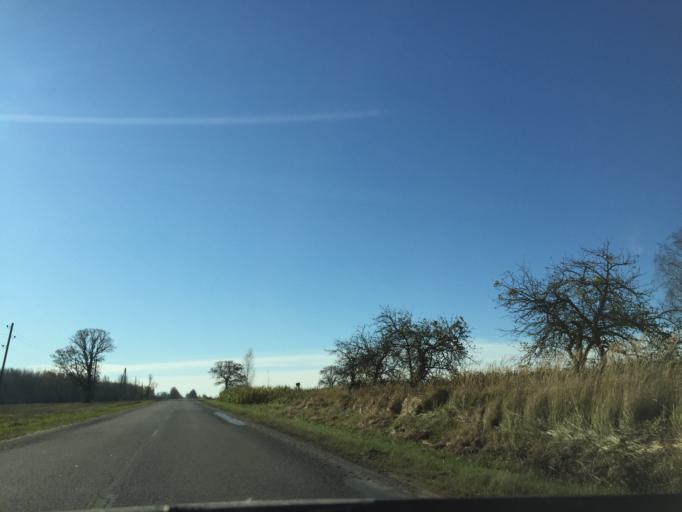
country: LV
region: Skriveri
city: Skriveri
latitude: 56.6998
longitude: 25.1509
